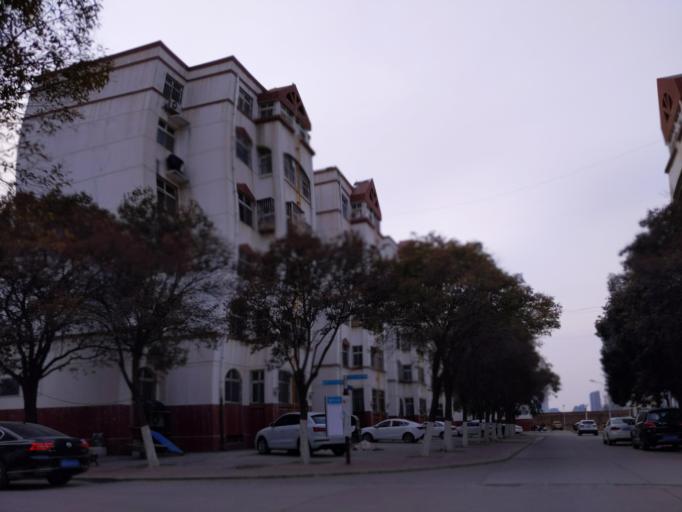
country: CN
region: Henan Sheng
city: Zhongyuanlu
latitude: 35.7565
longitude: 115.0516
